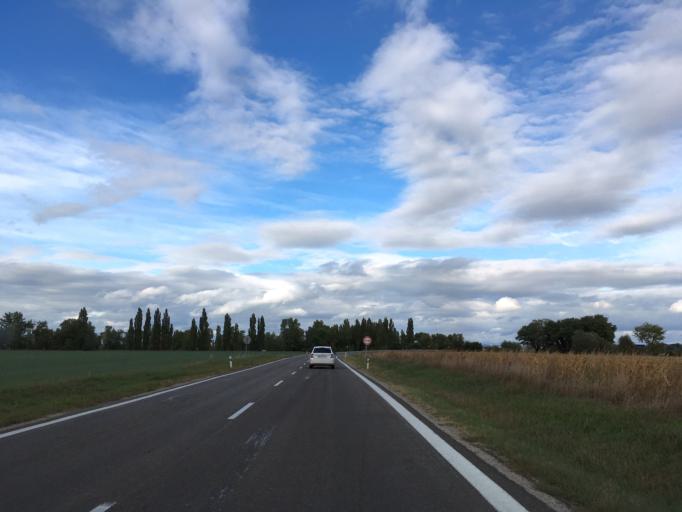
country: SK
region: Nitriansky
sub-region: Okres Nove Zamky
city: Nove Zamky
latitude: 47.9951
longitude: 18.2405
